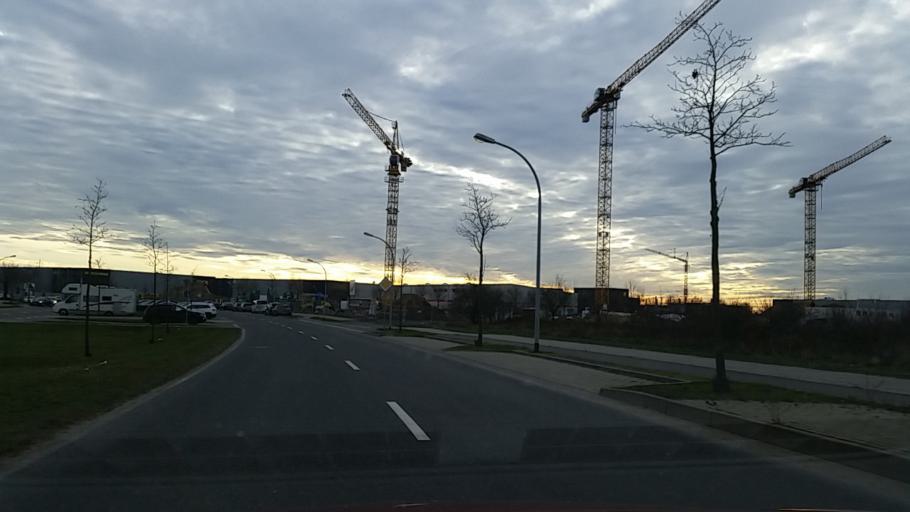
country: DE
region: Brandenburg
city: Schonefeld
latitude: 52.3907
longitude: 13.4982
